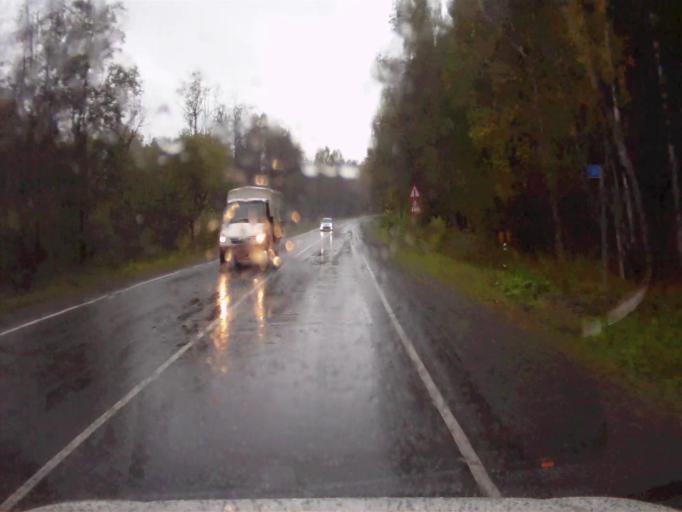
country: RU
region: Chelyabinsk
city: Kyshtym
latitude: 55.9057
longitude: 60.4424
